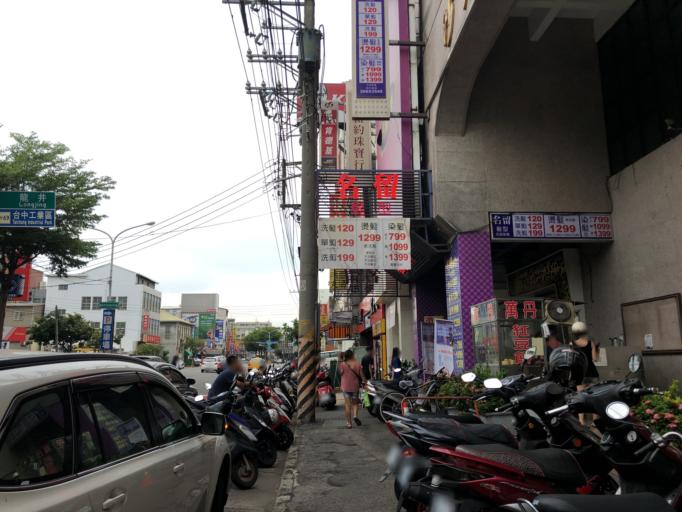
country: TW
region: Taiwan
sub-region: Taichung City
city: Taichung
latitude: 24.2361
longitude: 120.5592
